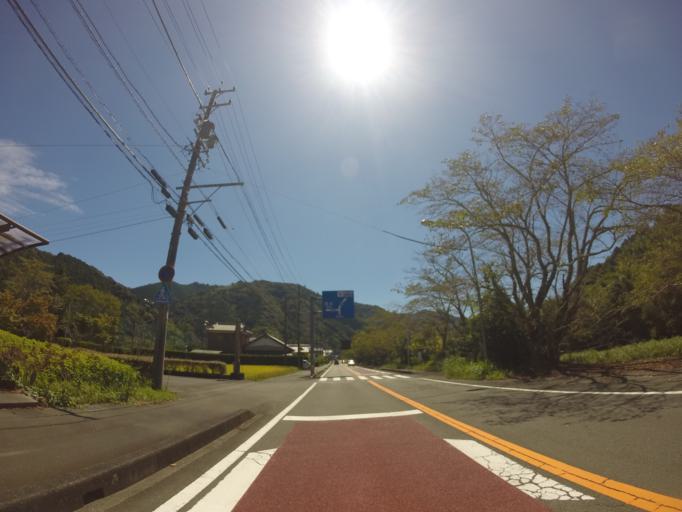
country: JP
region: Shizuoka
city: Fujieda
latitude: 34.9217
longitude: 138.2061
